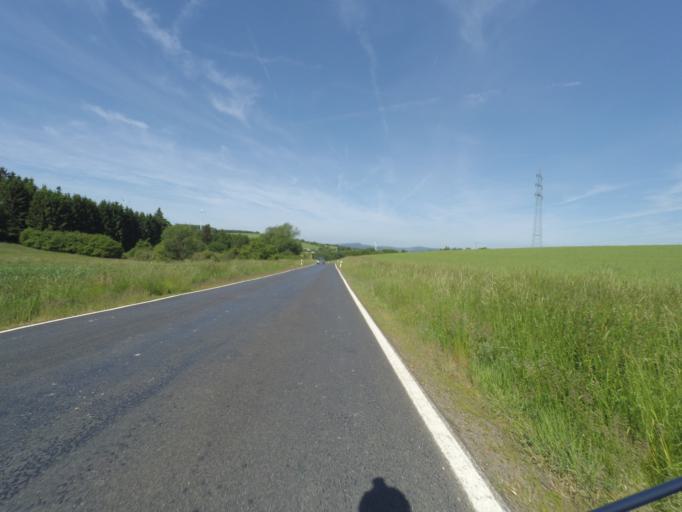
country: DE
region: Rheinland-Pfalz
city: Laubach
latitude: 50.2450
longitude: 7.0820
